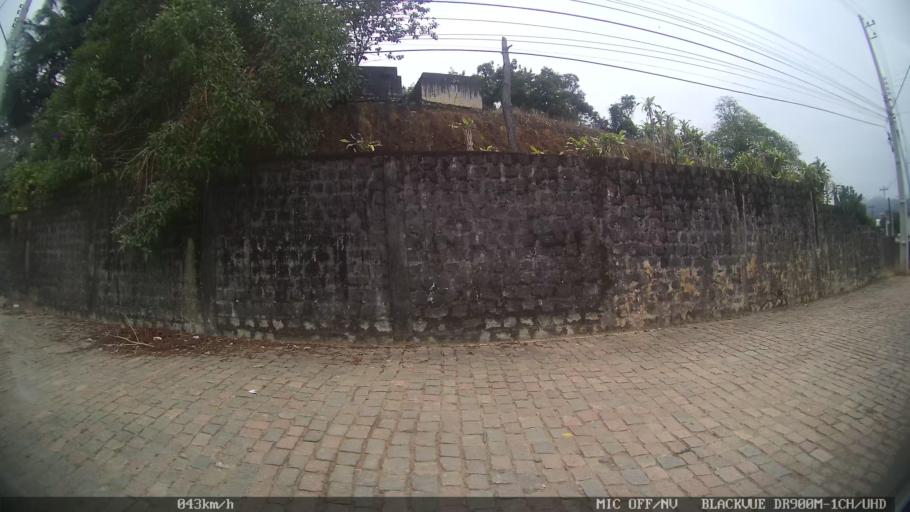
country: BR
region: Santa Catarina
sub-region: Joinville
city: Joinville
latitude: -26.2128
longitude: -48.9052
